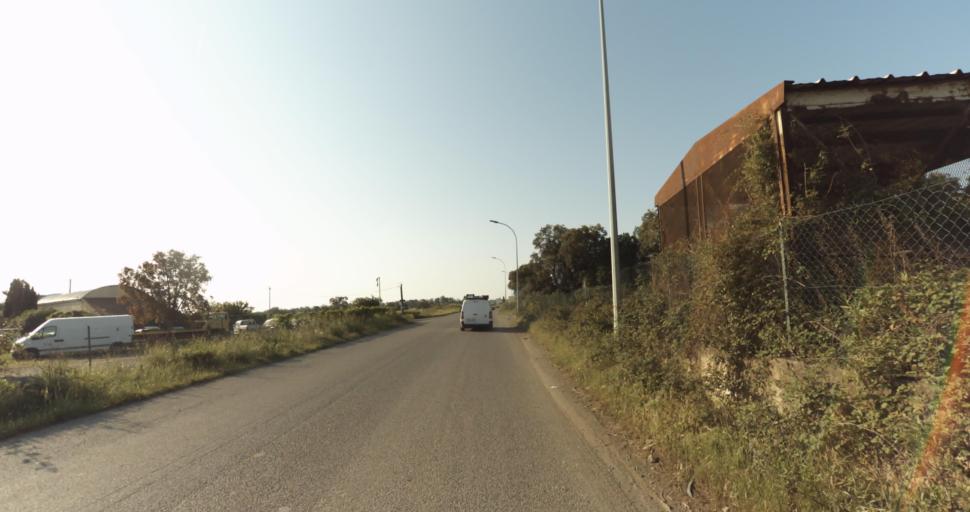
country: FR
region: Corsica
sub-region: Departement de la Haute-Corse
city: Biguglia
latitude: 42.5971
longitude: 9.4412
